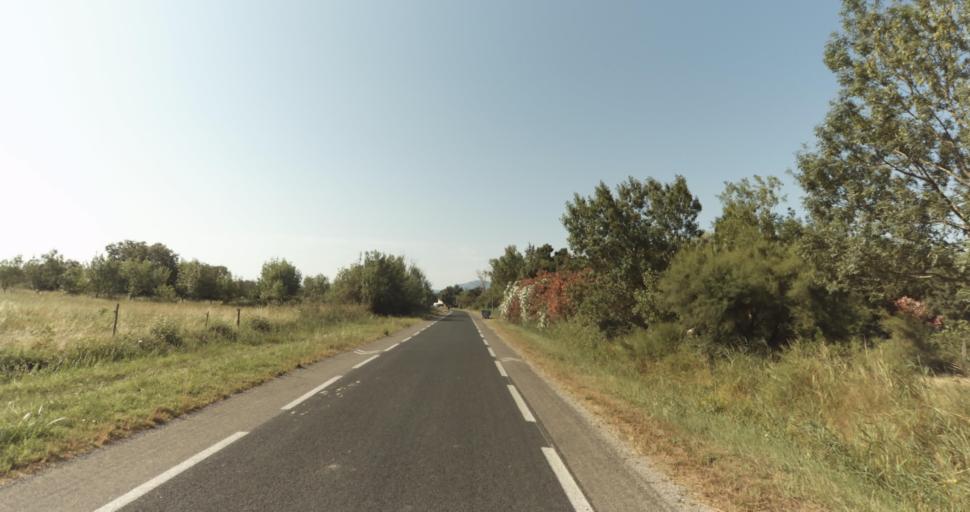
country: FR
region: Languedoc-Roussillon
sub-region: Departement des Pyrenees-Orientales
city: Saint-Cyprien-Plage
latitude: 42.6283
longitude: 3.0191
